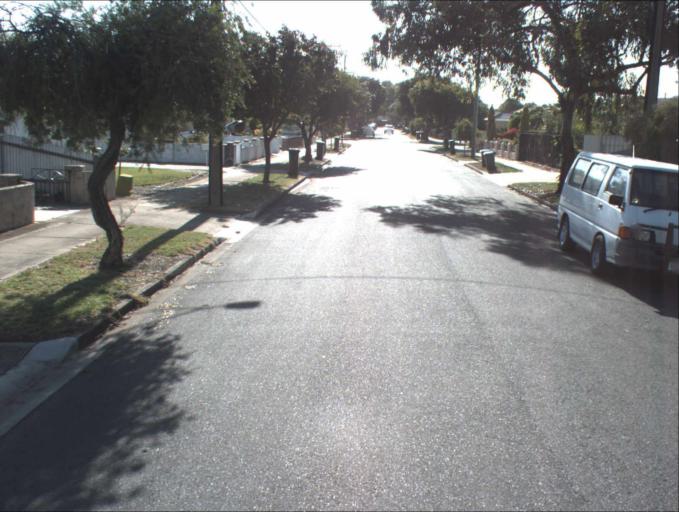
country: AU
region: South Australia
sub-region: Prospect
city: Prospect
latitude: -34.8851
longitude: 138.5728
